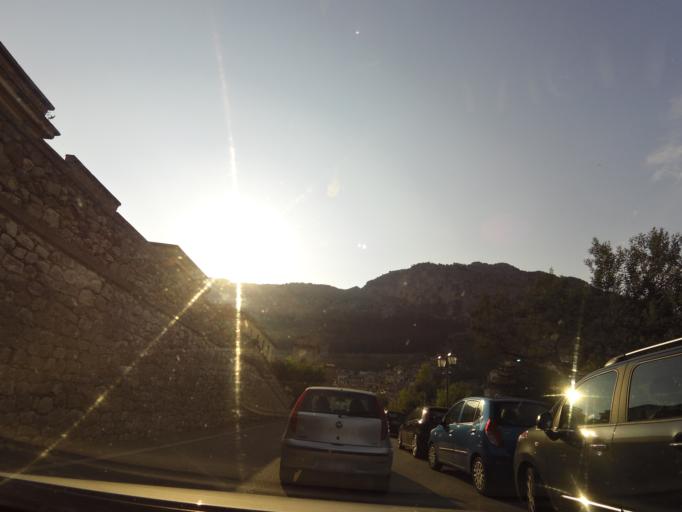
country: IT
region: Calabria
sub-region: Provincia di Reggio Calabria
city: Stilo
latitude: 38.4768
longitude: 16.4707
